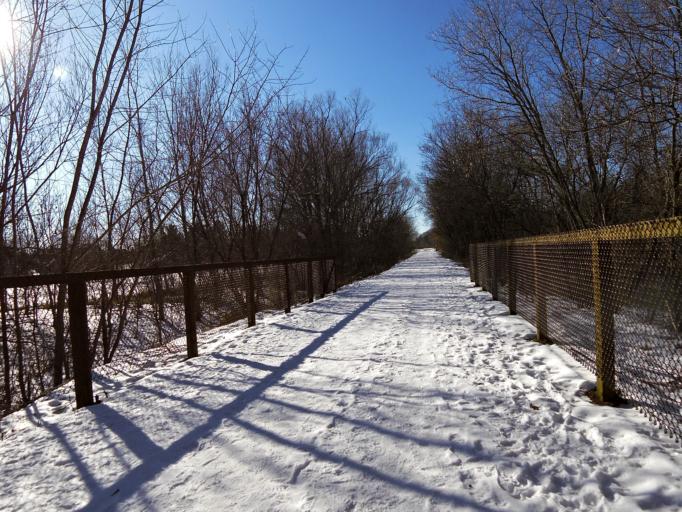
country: US
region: Minnesota
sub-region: Washington County
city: Stillwater
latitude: 45.0704
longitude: -92.8410
